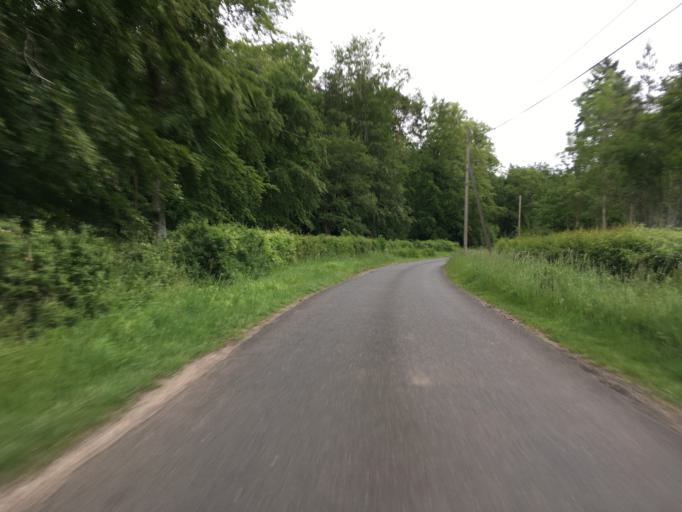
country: GB
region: England
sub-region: Wiltshire
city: Luckington
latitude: 51.5763
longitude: -2.2884
